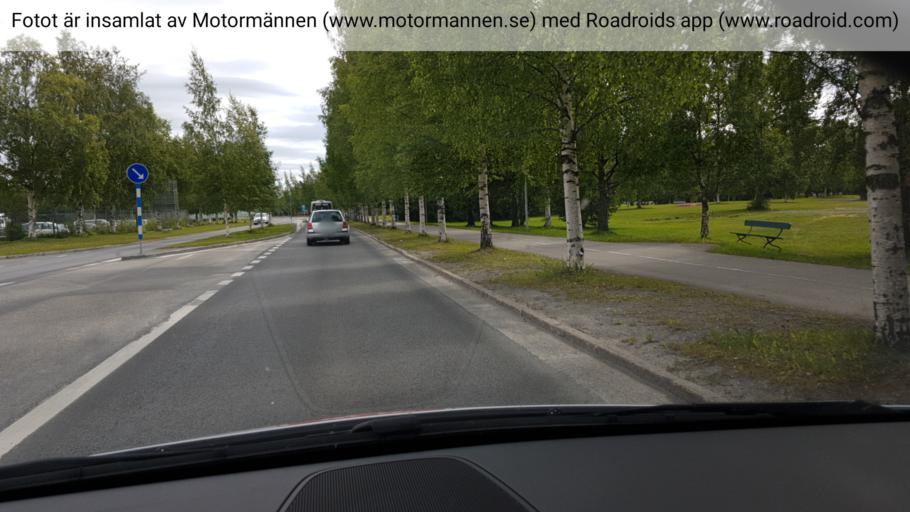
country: SE
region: Jaemtland
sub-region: OEstersunds Kommun
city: Ostersund
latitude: 63.1752
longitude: 14.6631
